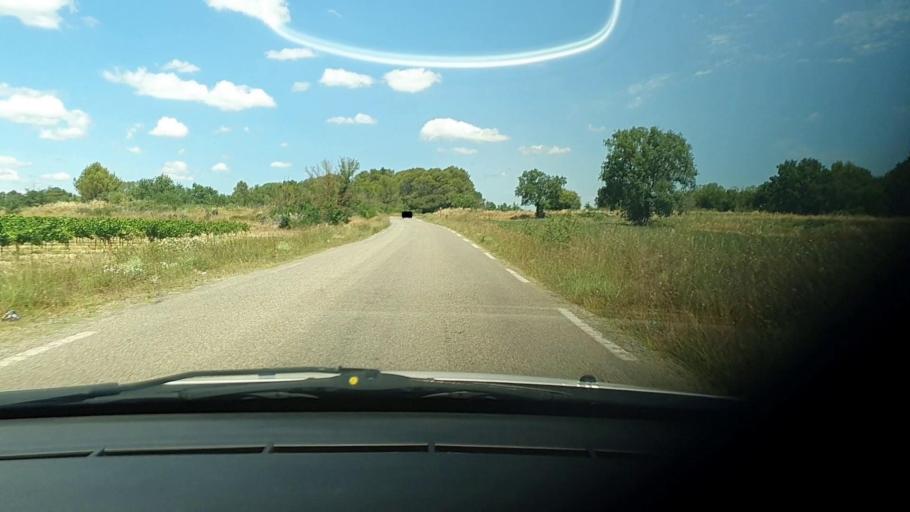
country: FR
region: Languedoc-Roussillon
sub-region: Departement du Gard
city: Blauzac
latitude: 43.9722
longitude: 4.3685
